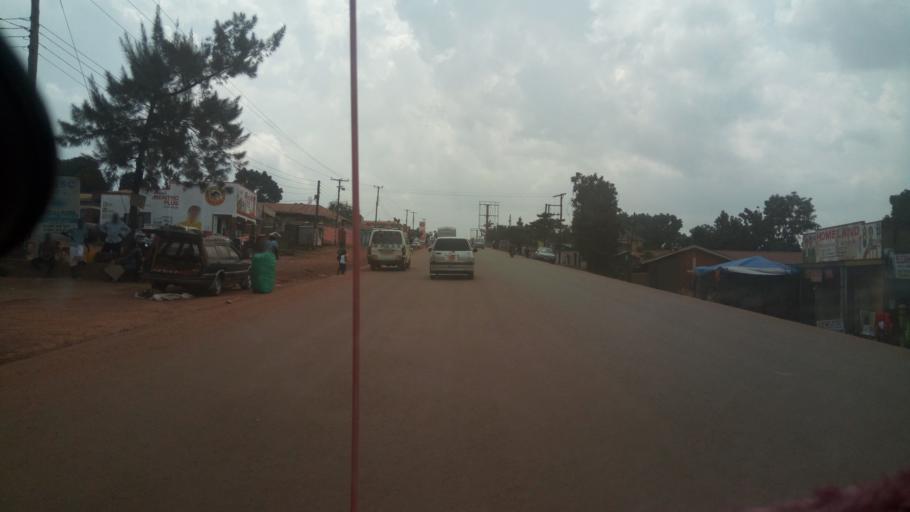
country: UG
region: Central Region
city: Kampala Central Division
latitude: 0.3536
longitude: 32.5361
